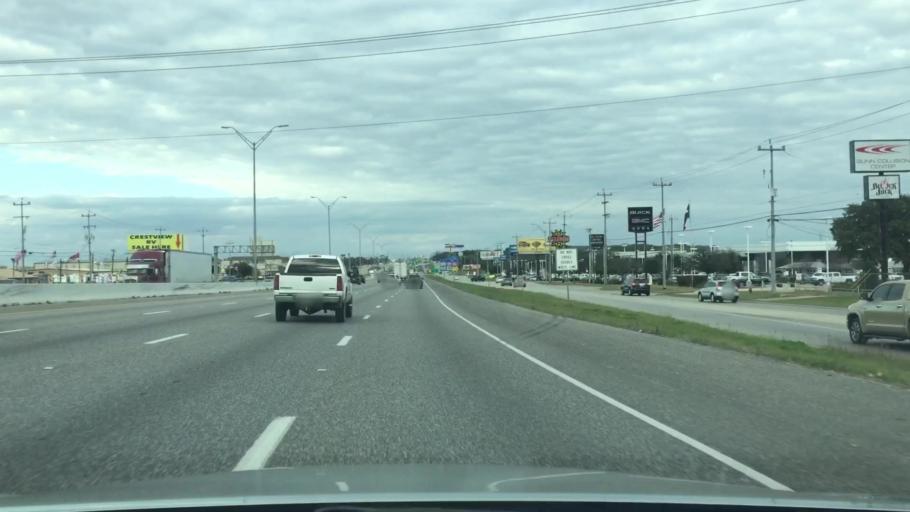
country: US
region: Texas
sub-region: Bexar County
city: Selma
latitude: 29.5890
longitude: -98.3007
